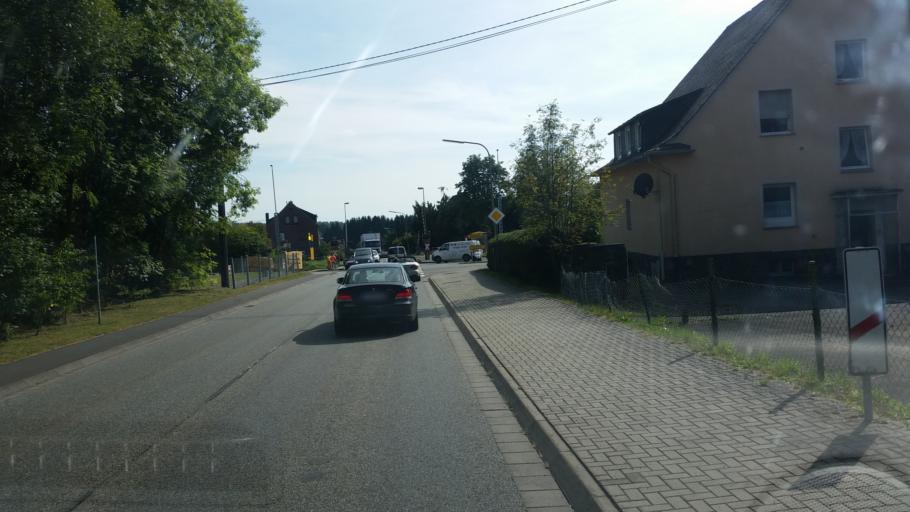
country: DE
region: Rheinland-Pfalz
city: Langenhahn
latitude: 50.5883
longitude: 7.9167
